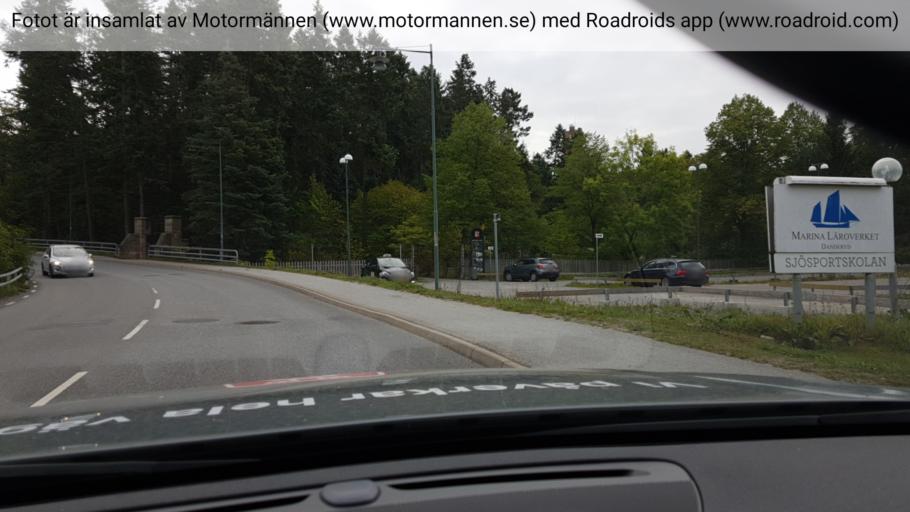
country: SE
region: Stockholm
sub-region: Danderyds Kommun
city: Djursholm
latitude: 59.3822
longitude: 18.0521
